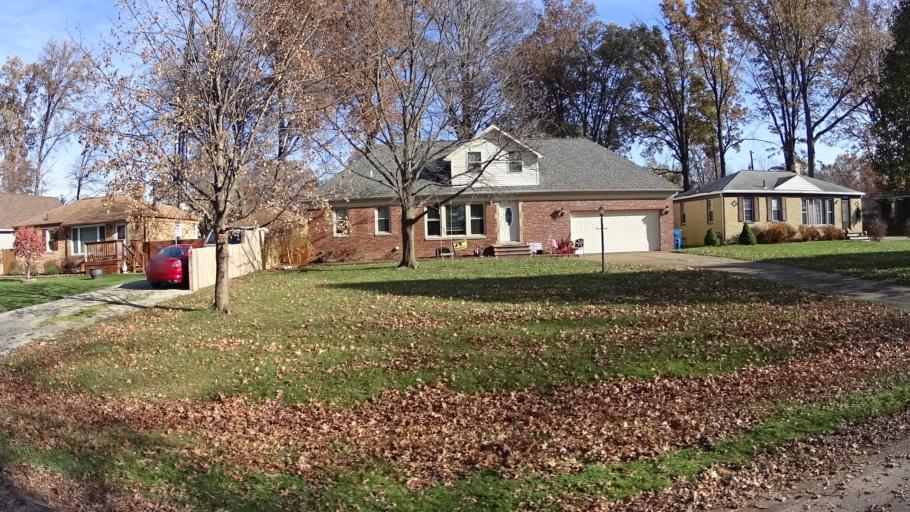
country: US
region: Ohio
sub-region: Lorain County
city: Avon
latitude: 41.4624
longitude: -82.0375
